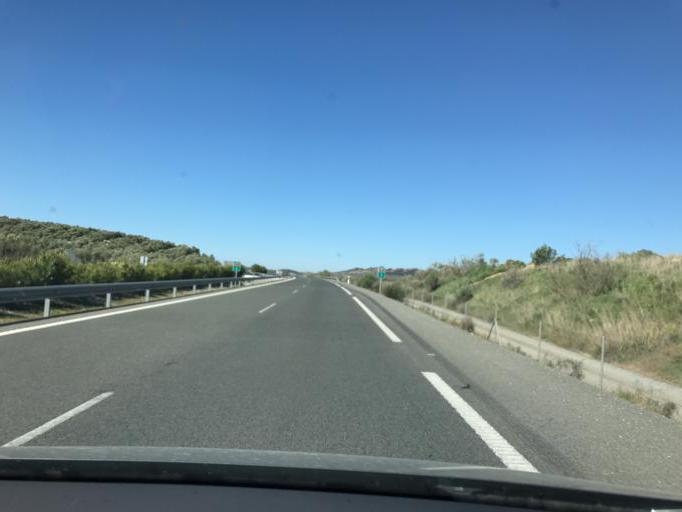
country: ES
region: Andalusia
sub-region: Provincia de Malaga
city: Villanueva del Trabuco
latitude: 37.0661
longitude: -4.3361
